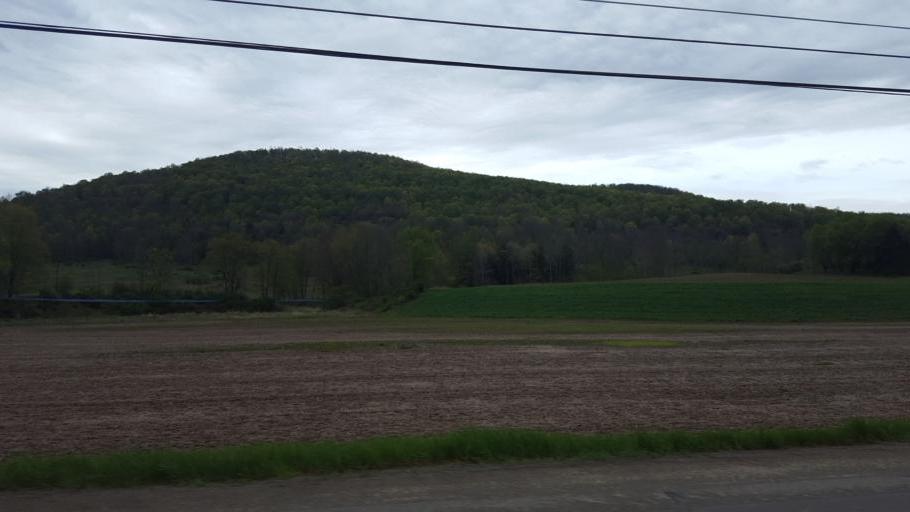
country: US
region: Pennsylvania
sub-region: Tioga County
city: Westfield
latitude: 41.9137
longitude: -77.5817
